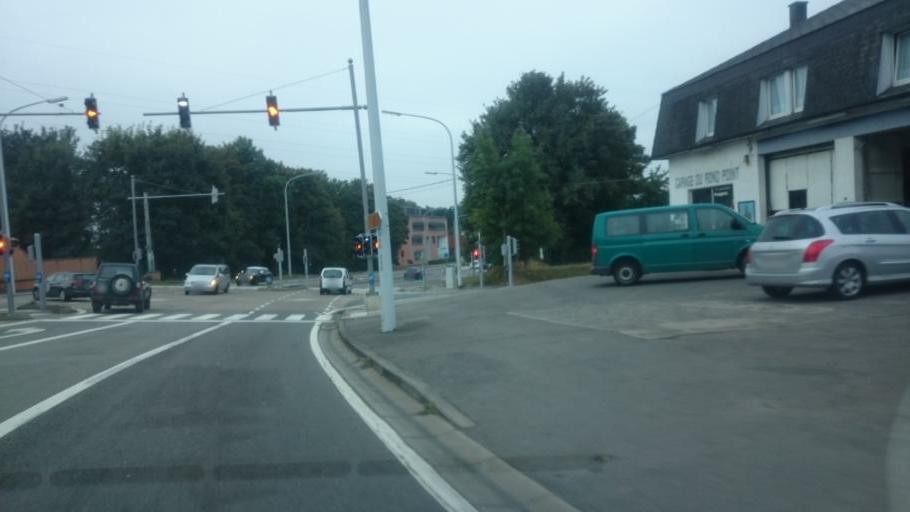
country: BE
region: Wallonia
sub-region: Province de Namur
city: Namur
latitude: 50.4881
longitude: 4.8932
